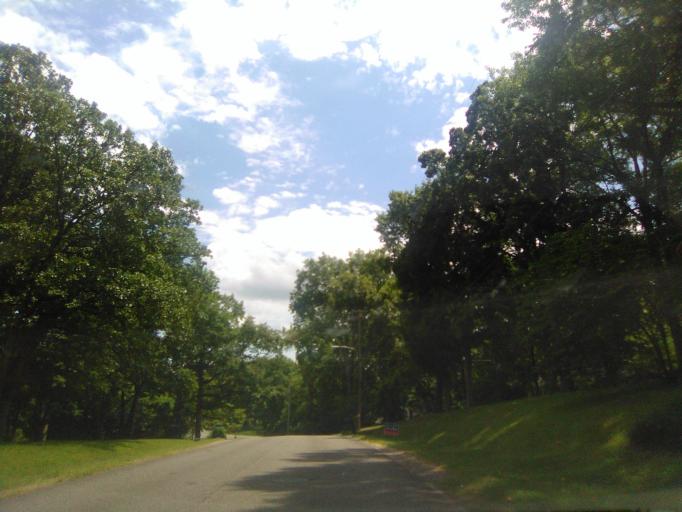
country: US
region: Tennessee
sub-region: Davidson County
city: Belle Meade
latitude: 36.1259
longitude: -86.8821
